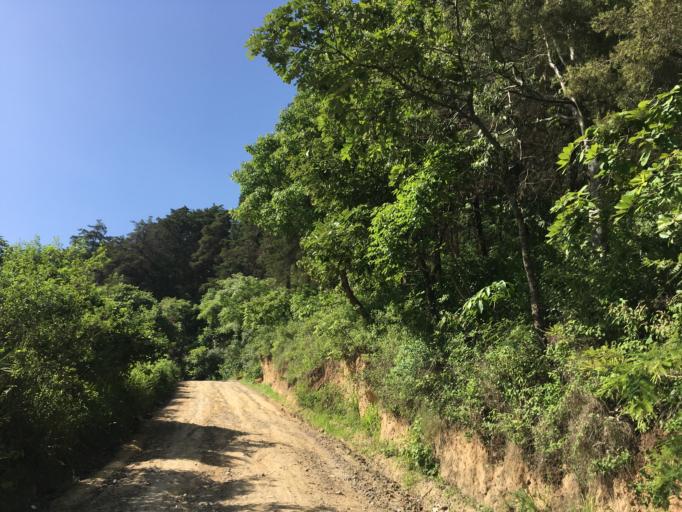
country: GT
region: Guatemala
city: Petapa
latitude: 14.4851
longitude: -90.5529
